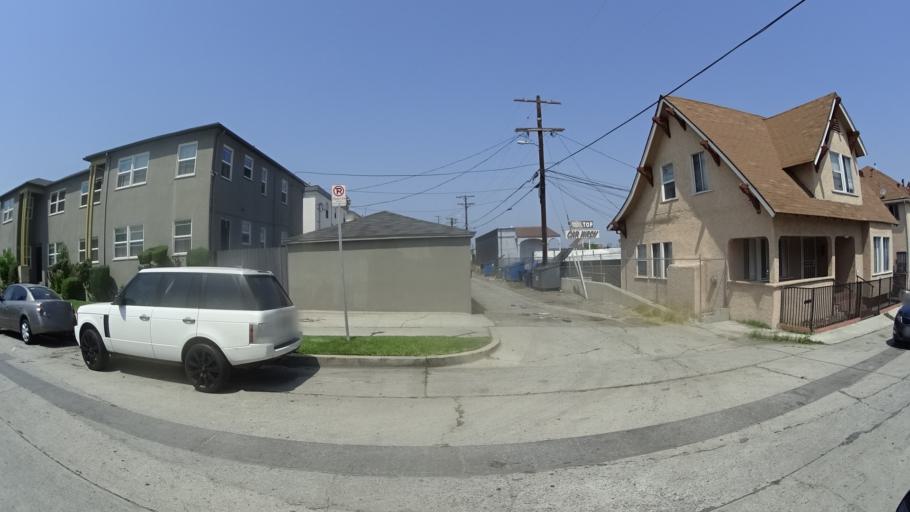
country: US
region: California
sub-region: Los Angeles County
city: Inglewood
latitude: 33.9738
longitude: -118.3288
